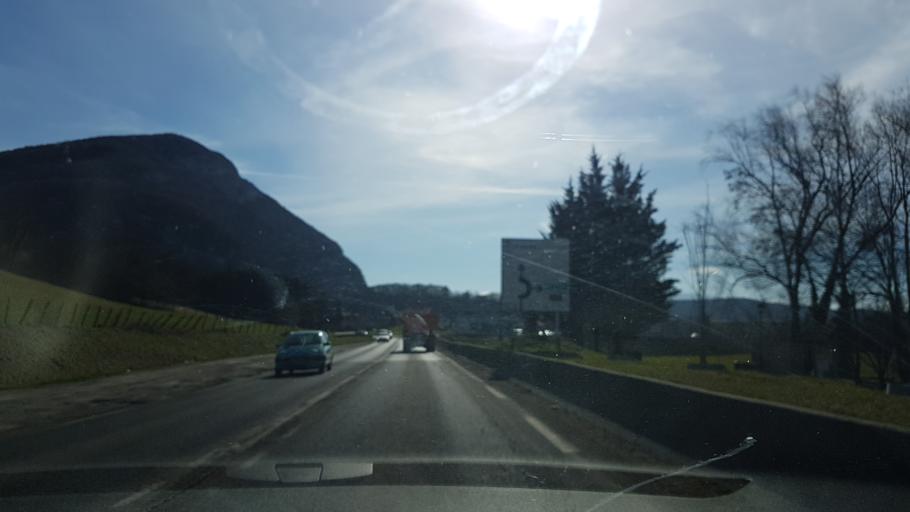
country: FR
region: Rhone-Alpes
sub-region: Departement de la Haute-Savoie
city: La Balme-de-Sillingy
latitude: 45.9660
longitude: 6.0358
